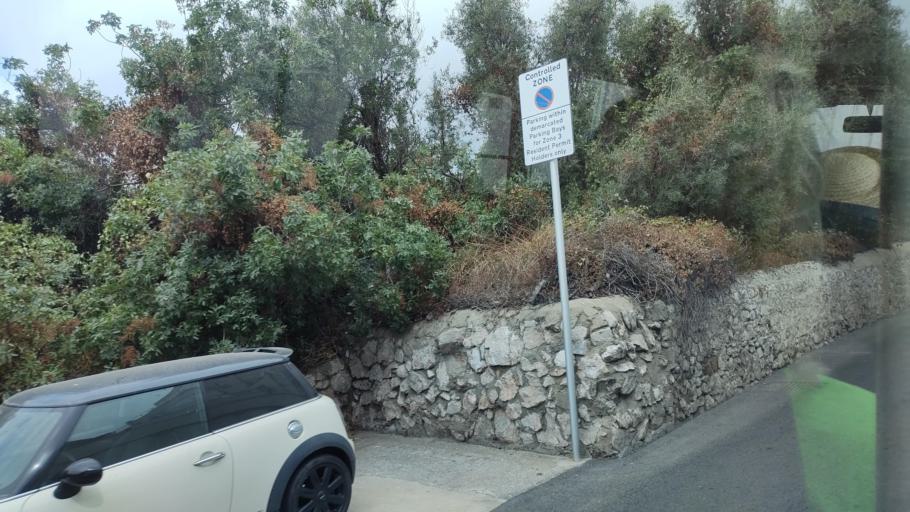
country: GI
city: Gibraltar
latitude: 36.1178
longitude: -5.3482
